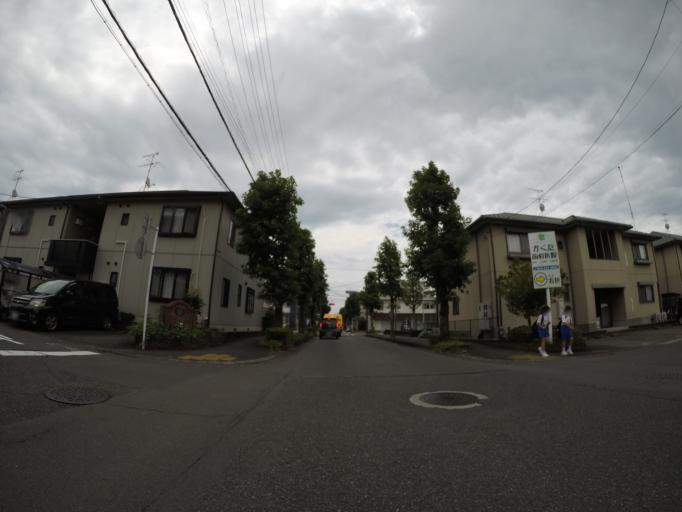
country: JP
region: Shizuoka
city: Shizuoka-shi
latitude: 34.9529
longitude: 138.4191
